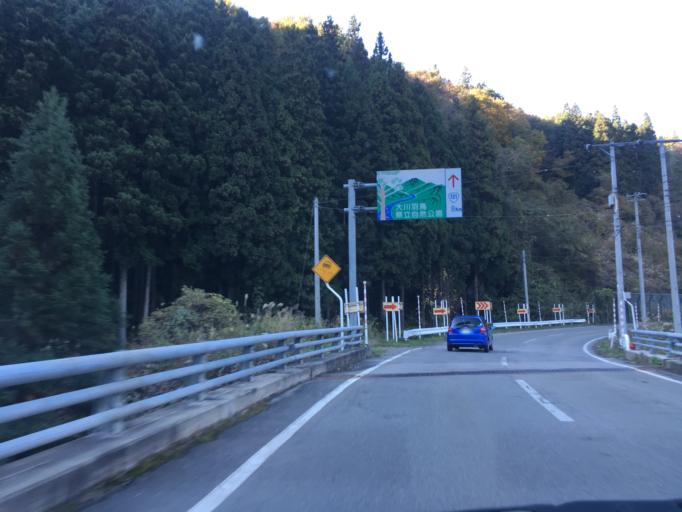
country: JP
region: Fukushima
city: Inawashiro
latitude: 37.2887
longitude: 139.9611
